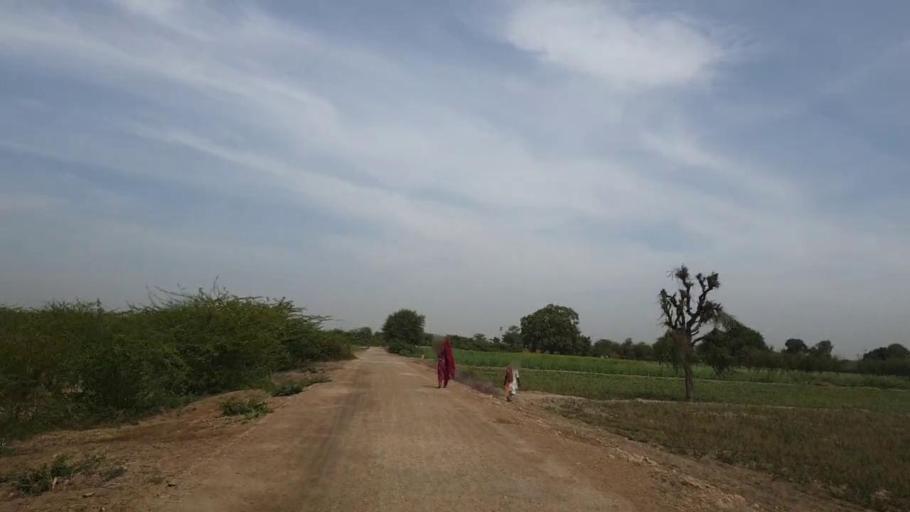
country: PK
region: Sindh
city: Kunri
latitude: 25.1862
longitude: 69.6016
